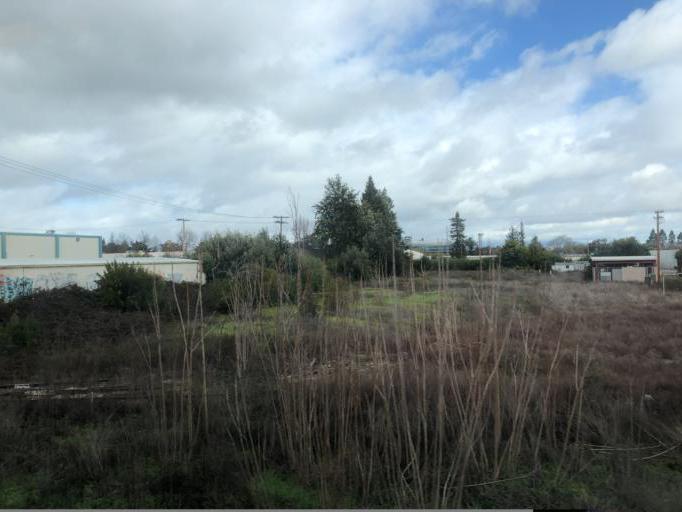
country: US
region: California
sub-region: Santa Clara County
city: Sunnyvale
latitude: 37.3727
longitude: -122.0101
